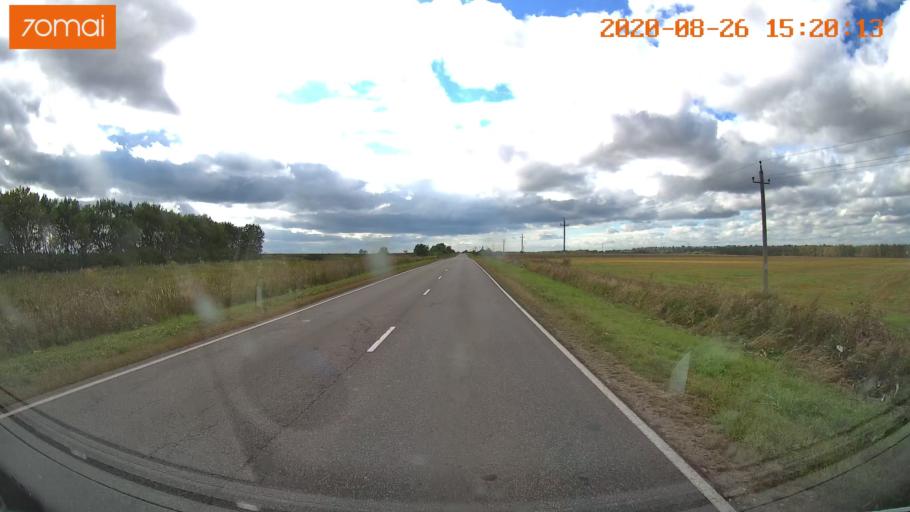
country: RU
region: Tula
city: Severo-Zadonsk
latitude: 54.1424
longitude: 38.5023
